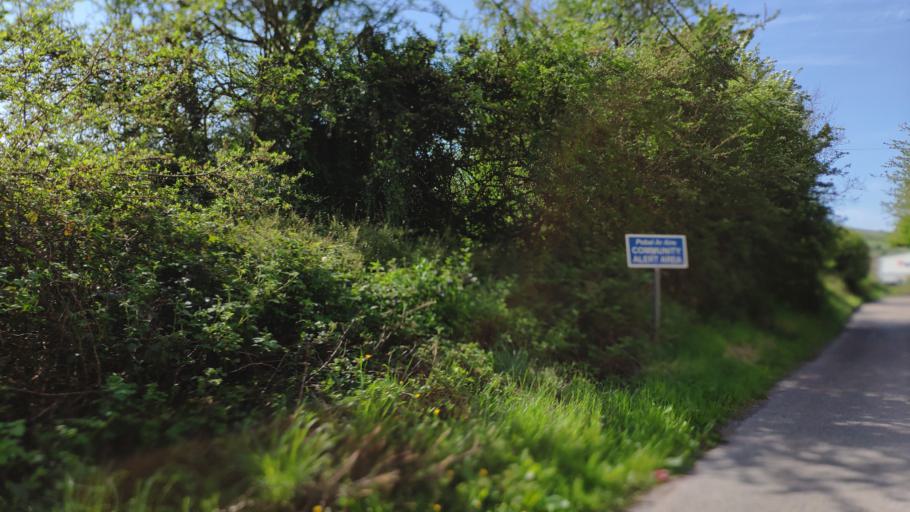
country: IE
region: Munster
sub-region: County Cork
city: Cork
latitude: 51.9212
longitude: -8.5007
